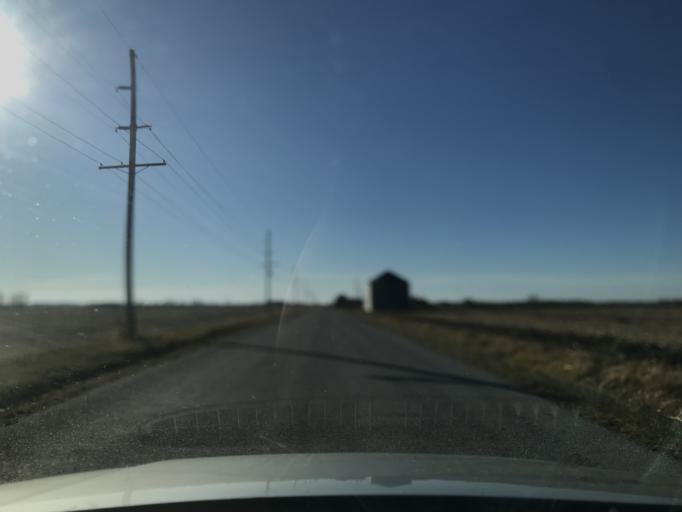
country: US
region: Illinois
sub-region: Hancock County
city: Carthage
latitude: 40.4733
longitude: -91.1782
